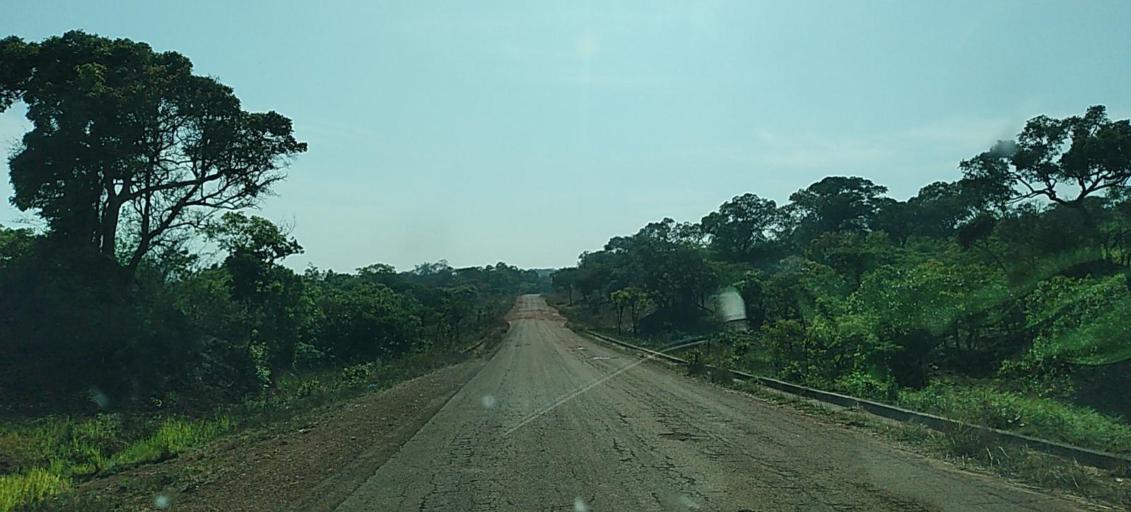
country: ZM
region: North-Western
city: Mwinilunga
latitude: -11.7853
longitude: 25.0381
